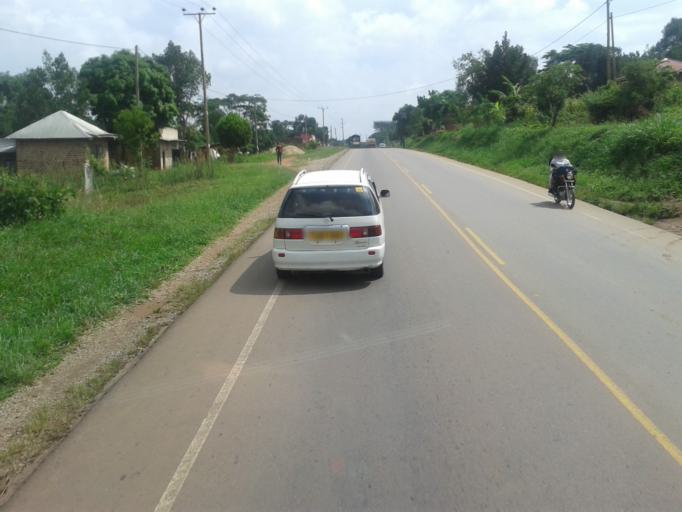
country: UG
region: Central Region
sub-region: Wakiso District
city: Wakiso
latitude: 0.5152
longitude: 32.5265
